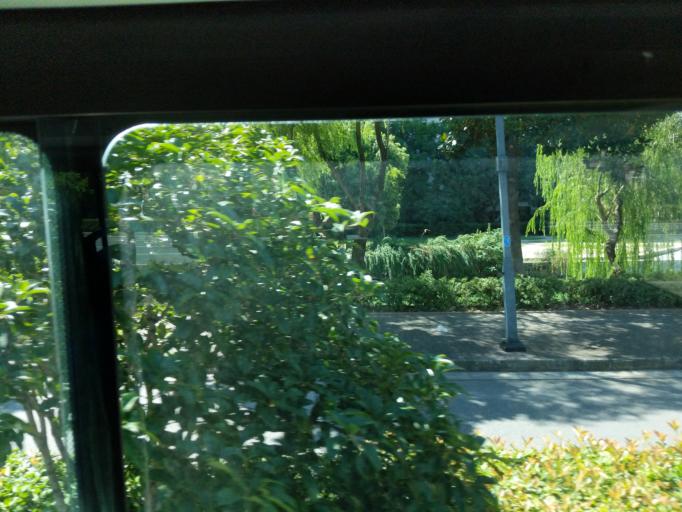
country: CN
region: Jiangsu Sheng
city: Pingjianglu
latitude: 31.3220
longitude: 120.6571
